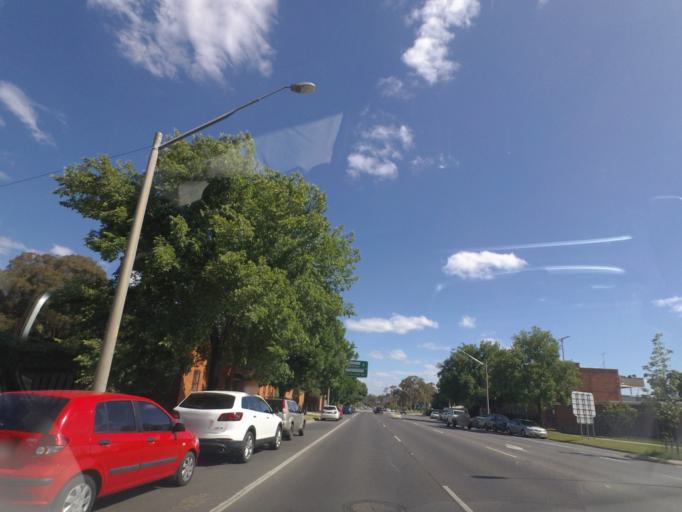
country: AU
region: New South Wales
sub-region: Albury Municipality
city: South Albury
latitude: -36.0826
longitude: 146.9101
